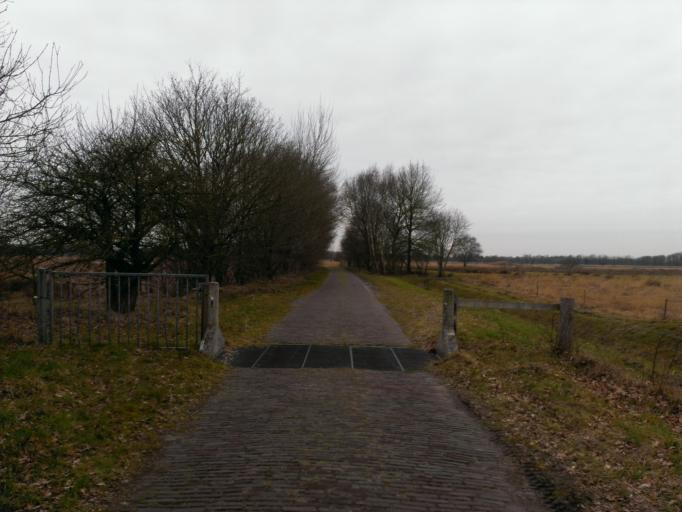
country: NL
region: Drenthe
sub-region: Gemeente Hoogeveen
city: Hoogeveen
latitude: 52.7583
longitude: 6.4854
